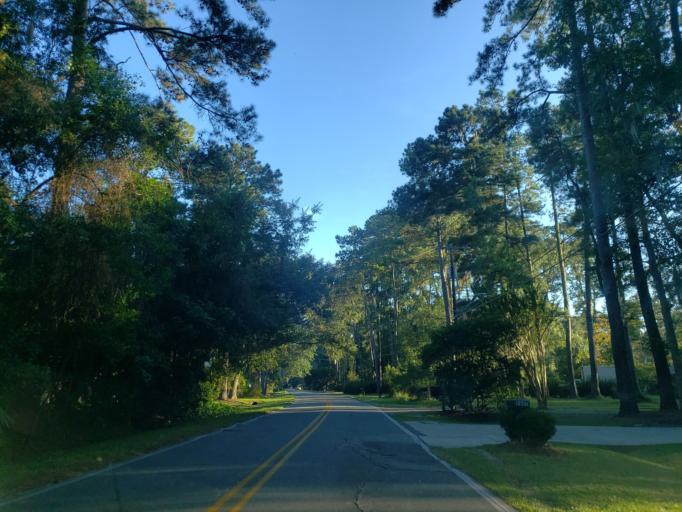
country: US
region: Georgia
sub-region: Chatham County
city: Isle of Hope
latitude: 31.9885
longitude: -81.0551
